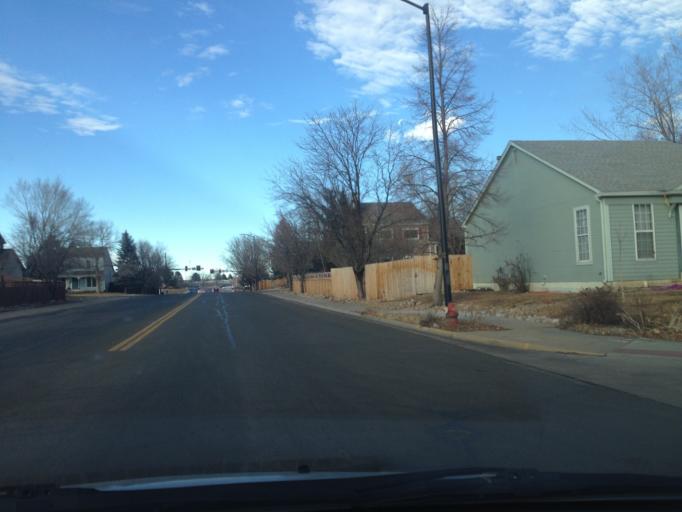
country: US
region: Colorado
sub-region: Boulder County
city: Lafayette
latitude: 39.9985
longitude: -105.1051
